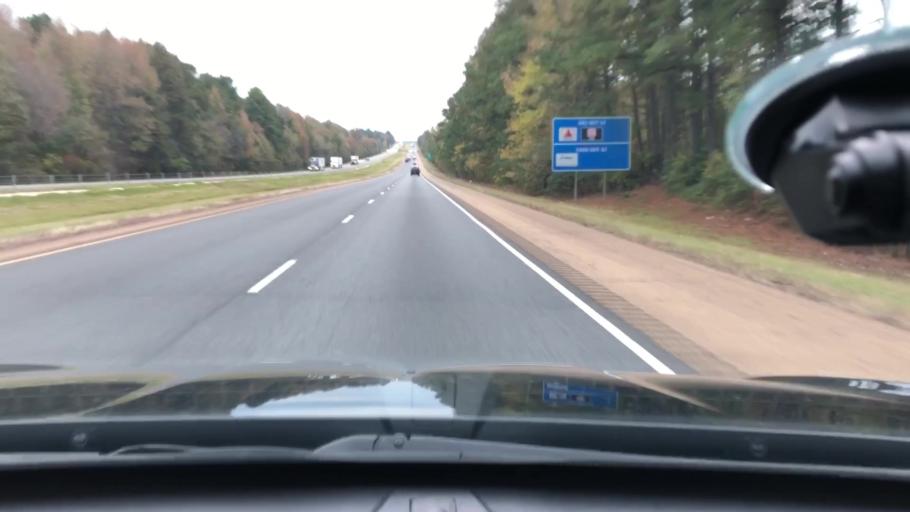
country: US
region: Arkansas
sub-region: Clark County
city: Gurdon
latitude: 33.9793
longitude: -93.2011
